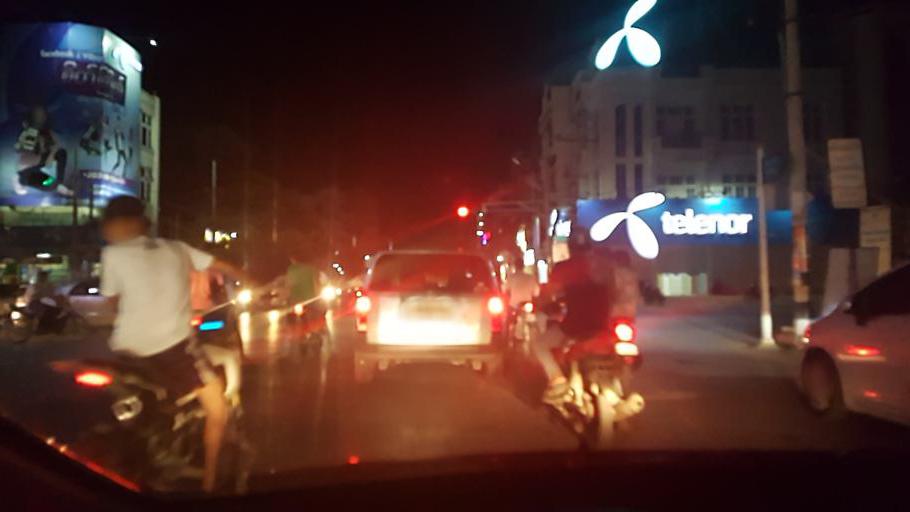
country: MM
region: Mandalay
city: Mandalay
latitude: 21.9762
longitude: 96.0956
